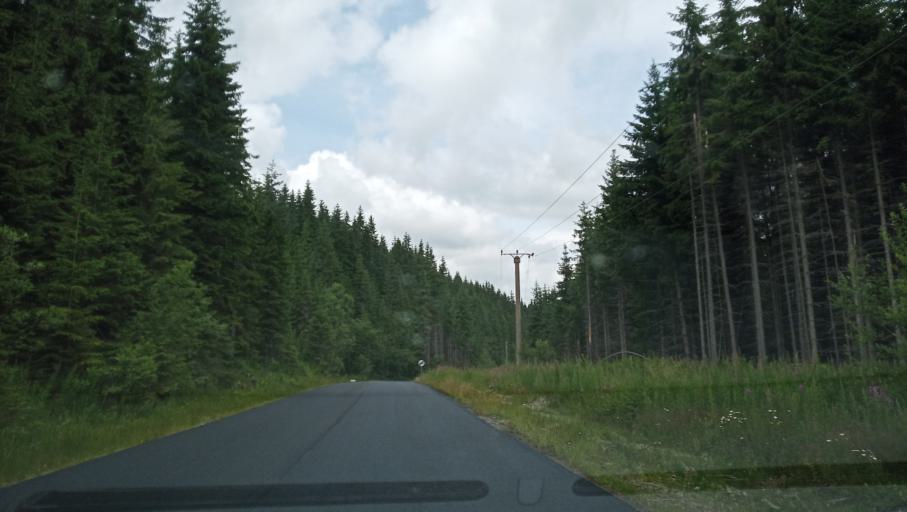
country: RO
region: Gorj
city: Novaci-Straini
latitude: 45.4239
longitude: 23.6924
